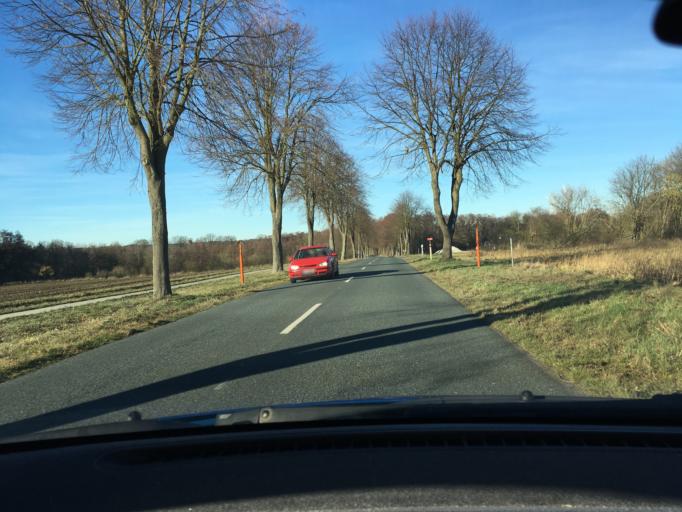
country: DE
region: Lower Saxony
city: Melbeck
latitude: 53.1666
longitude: 10.3824
